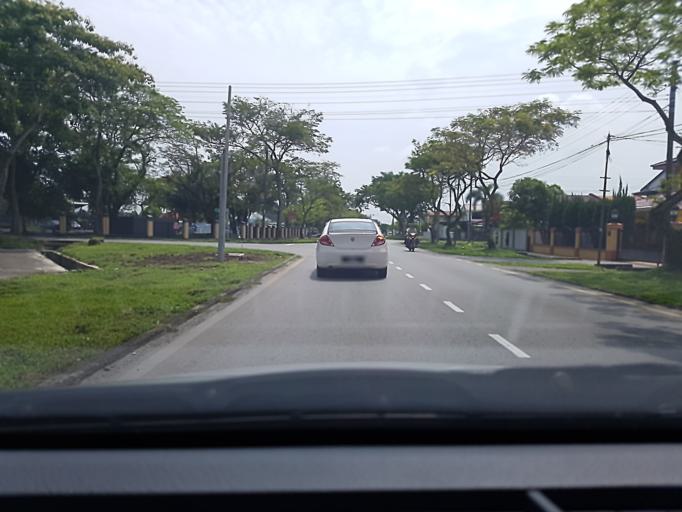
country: MY
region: Sarawak
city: Kuching
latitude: 1.5086
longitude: 110.3625
